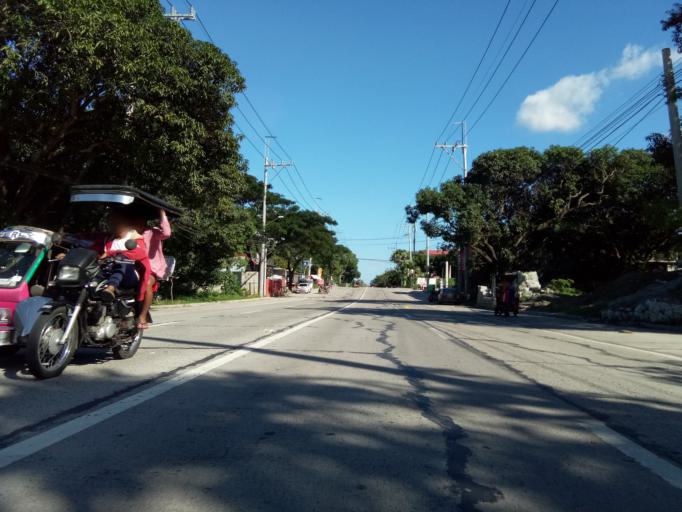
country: PH
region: Calabarzon
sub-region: Province of Cavite
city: Dasmarinas
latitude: 14.3519
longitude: 120.9507
